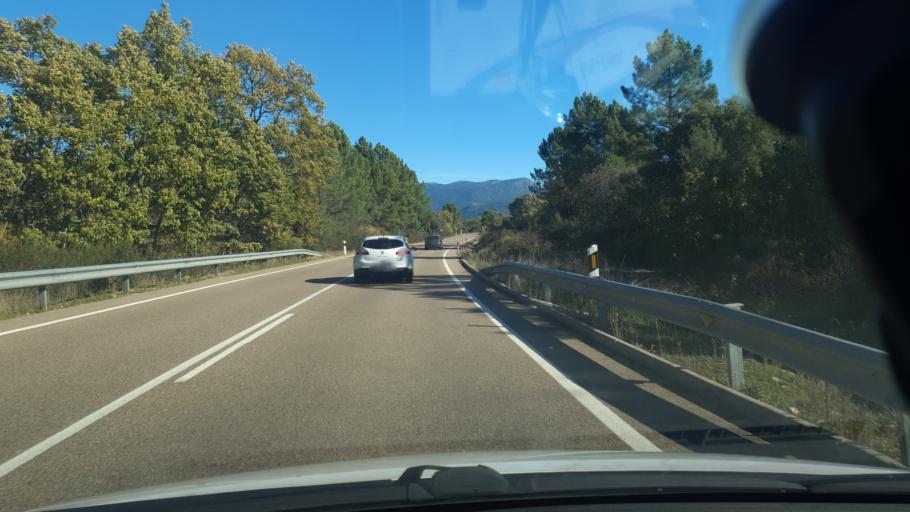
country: ES
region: Castille and Leon
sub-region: Provincia de Avila
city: Arenas de San Pedro
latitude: 40.1697
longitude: -5.1006
